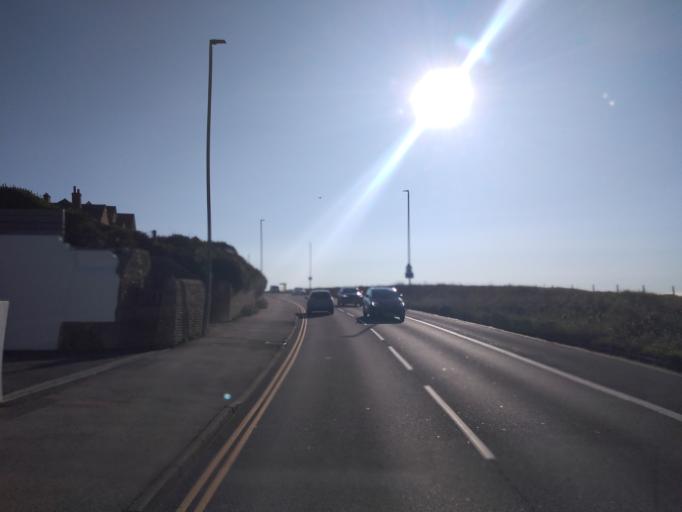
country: GB
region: England
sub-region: Brighton and Hove
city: Rottingdean
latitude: 50.8026
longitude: -0.0545
